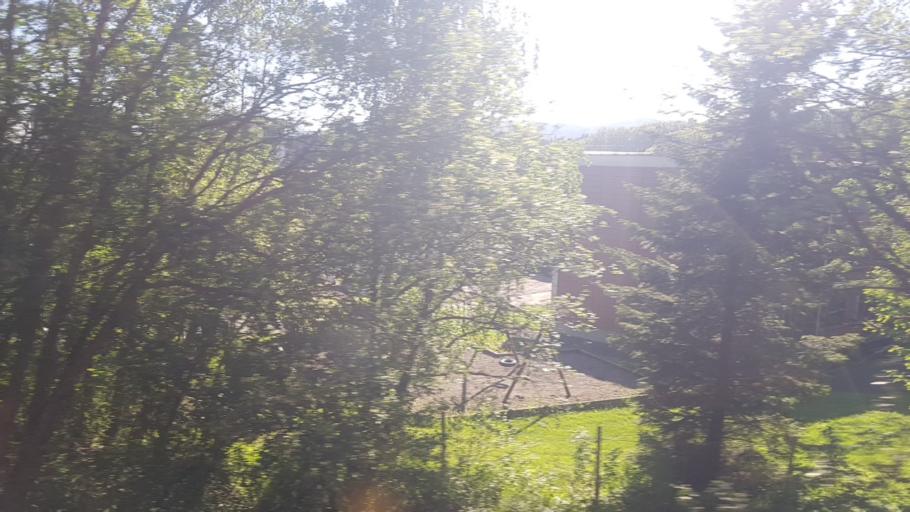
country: NO
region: Sor-Trondelag
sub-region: Trondheim
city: Trondheim
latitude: 63.3767
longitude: 10.3648
